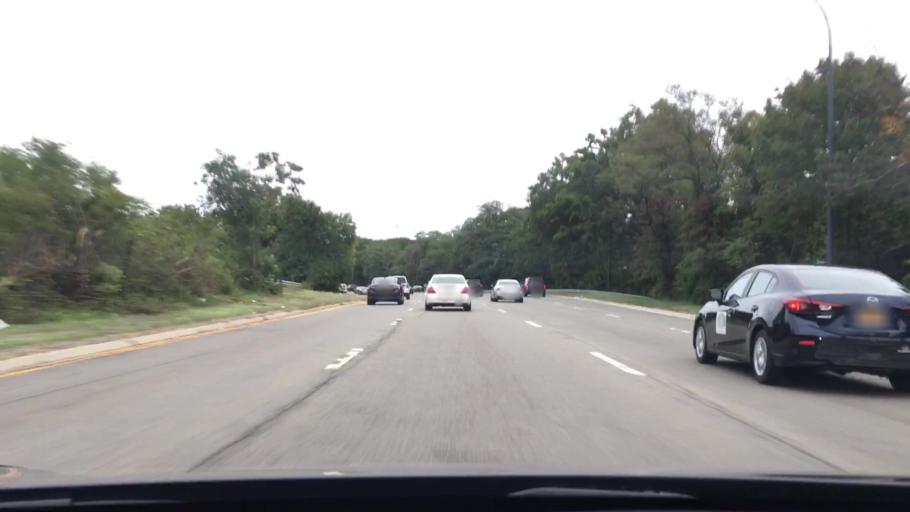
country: US
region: New York
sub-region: Nassau County
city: East Hills
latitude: 40.7763
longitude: -73.6249
